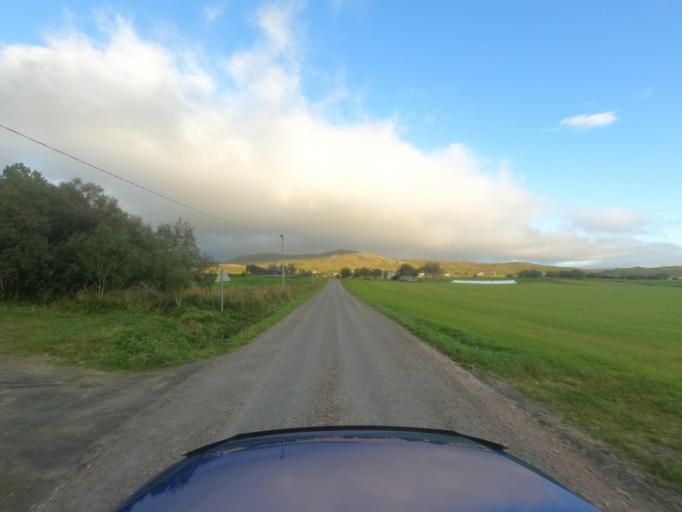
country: NO
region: Nordland
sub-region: Vestvagoy
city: Leknes
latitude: 68.2038
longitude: 13.6646
